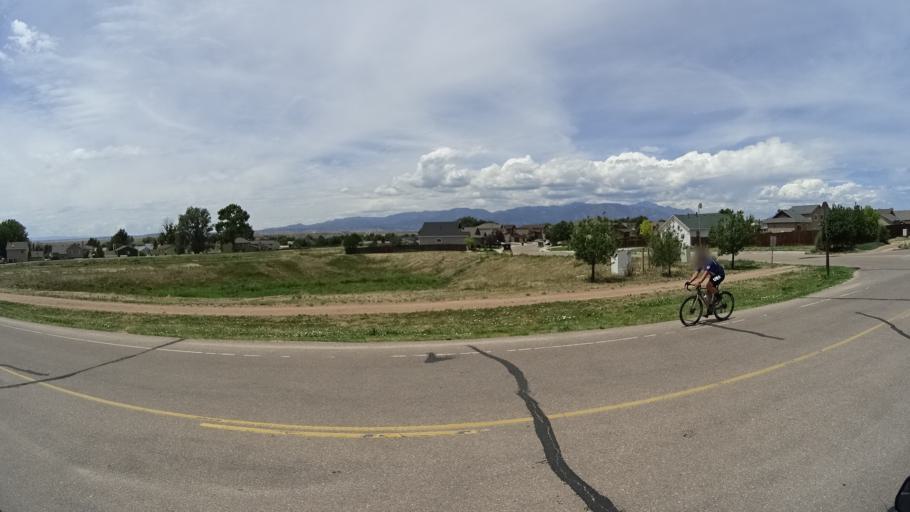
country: US
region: Colorado
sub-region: El Paso County
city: Fountain
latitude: 38.6721
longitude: -104.6733
